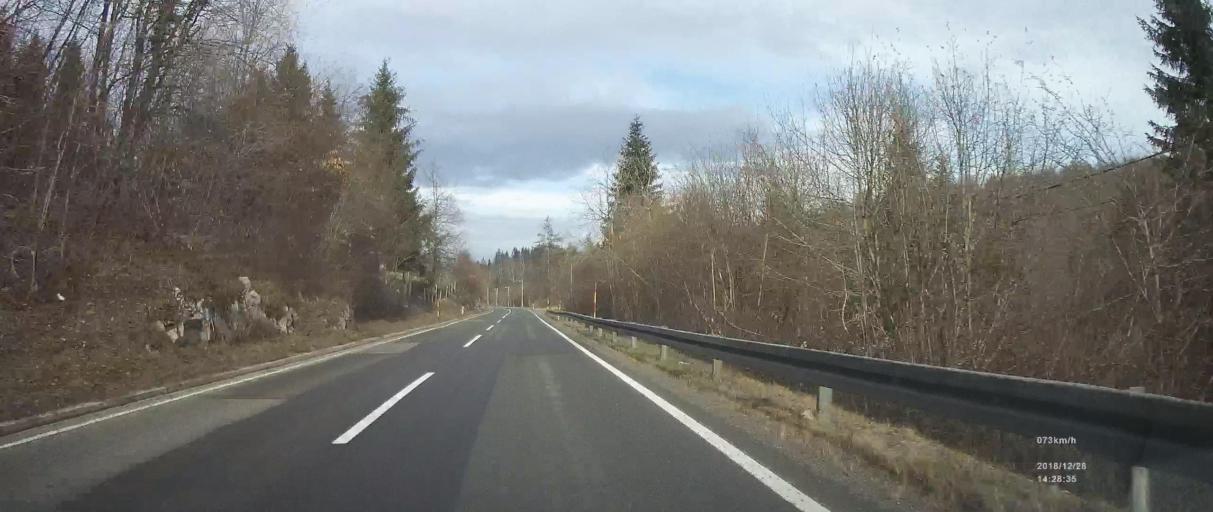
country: HR
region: Primorsko-Goranska
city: Vrbovsko
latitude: 45.4113
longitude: 15.1155
